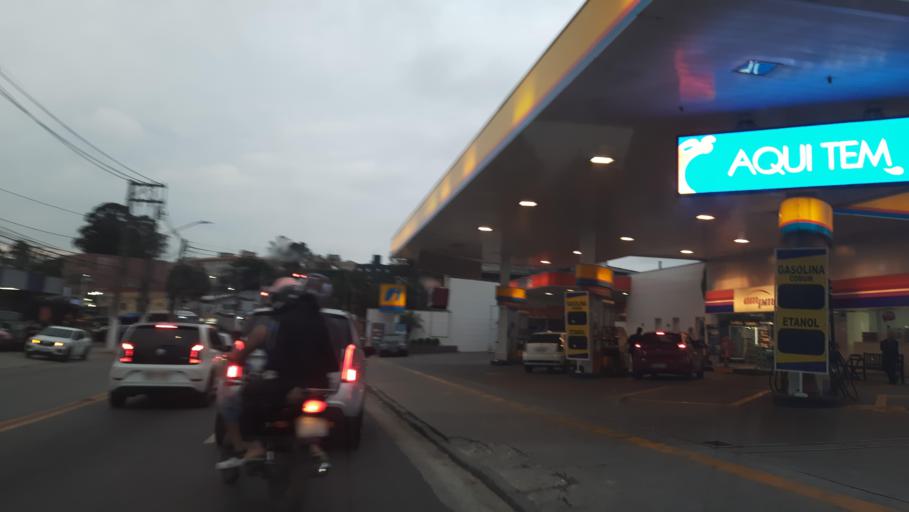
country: BR
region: Sao Paulo
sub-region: Caieiras
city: Caieiras
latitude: -23.4494
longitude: -46.7348
